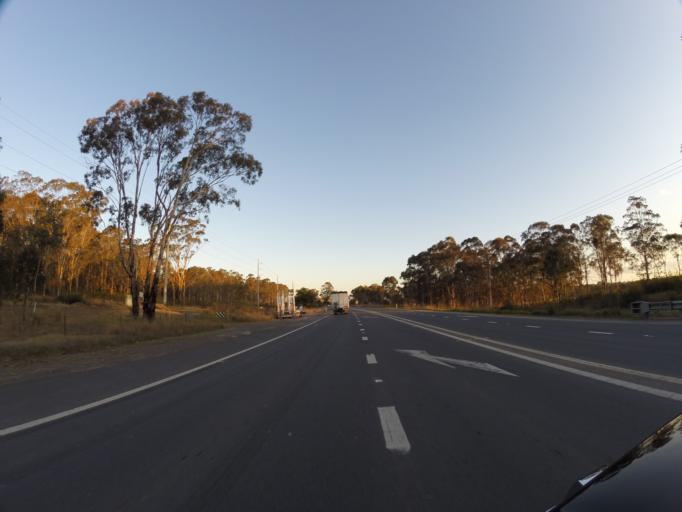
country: AU
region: New South Wales
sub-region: Camden
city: Narellan
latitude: -34.0149
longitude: 150.7241
